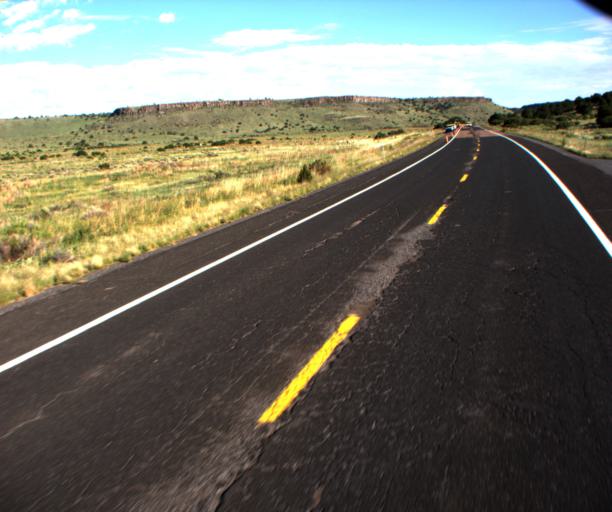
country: US
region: Arizona
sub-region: Apache County
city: Eagar
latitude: 34.0293
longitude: -109.1840
